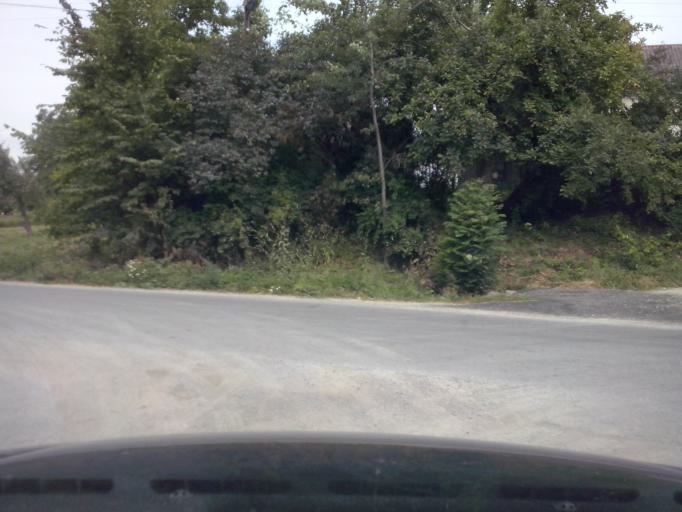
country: PL
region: Swietokrzyskie
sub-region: Powiat kielecki
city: Lagow
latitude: 50.7354
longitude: 21.0450
